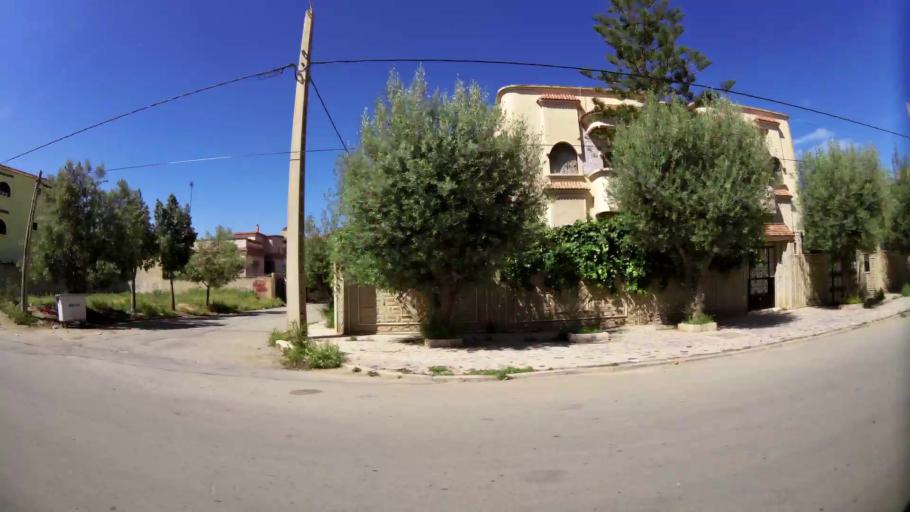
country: MA
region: Oriental
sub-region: Oujda-Angad
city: Oujda
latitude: 34.6652
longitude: -1.9292
